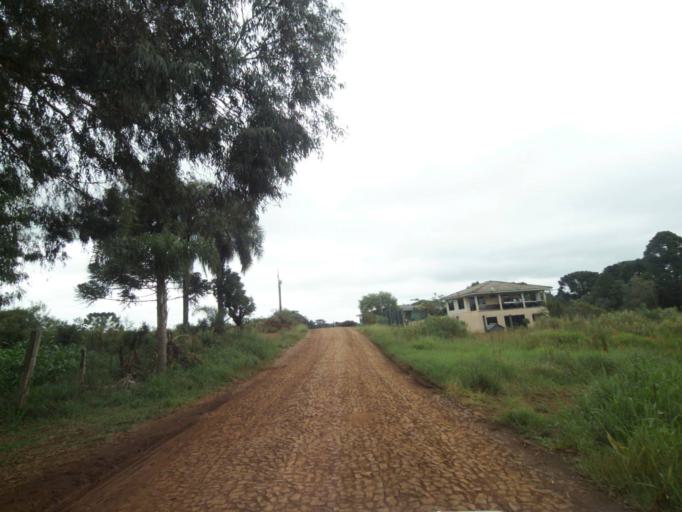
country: BR
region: Parana
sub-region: Pitanga
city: Pitanga
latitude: -24.9362
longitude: -51.8671
